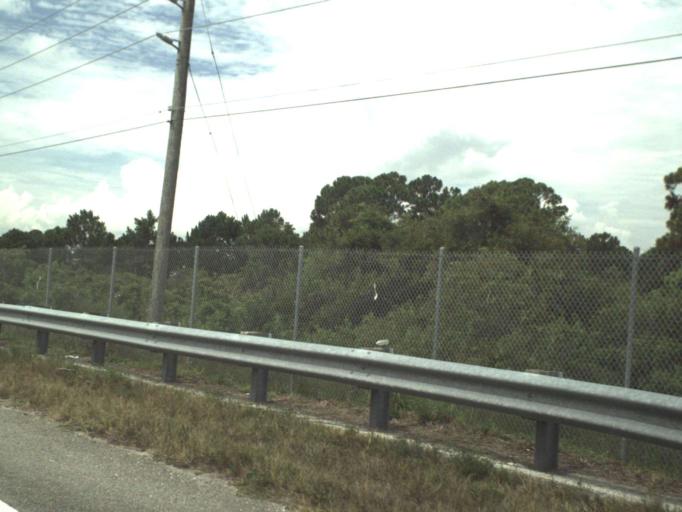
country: US
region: Florida
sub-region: Saint Lucie County
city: Fort Pierce North
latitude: 27.4957
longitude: -80.3498
